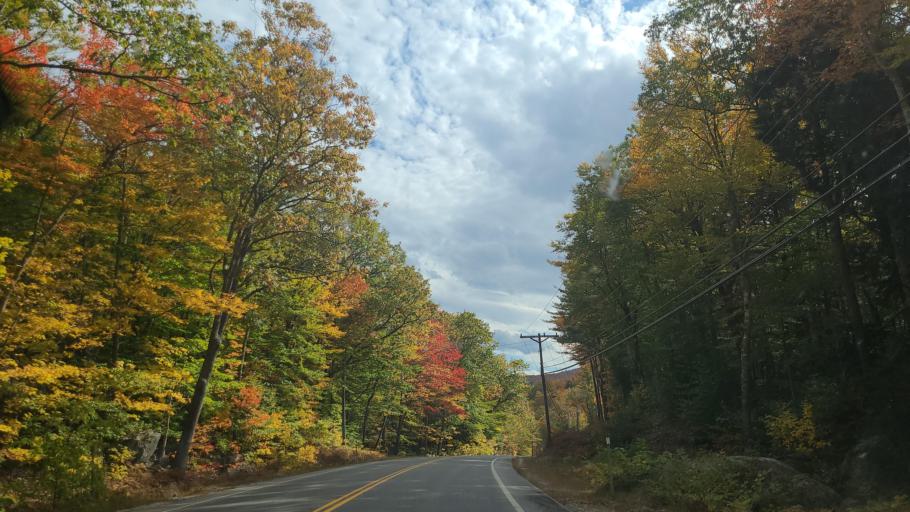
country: US
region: New Hampshire
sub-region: Carroll County
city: North Conway
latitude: 44.1683
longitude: -71.2233
